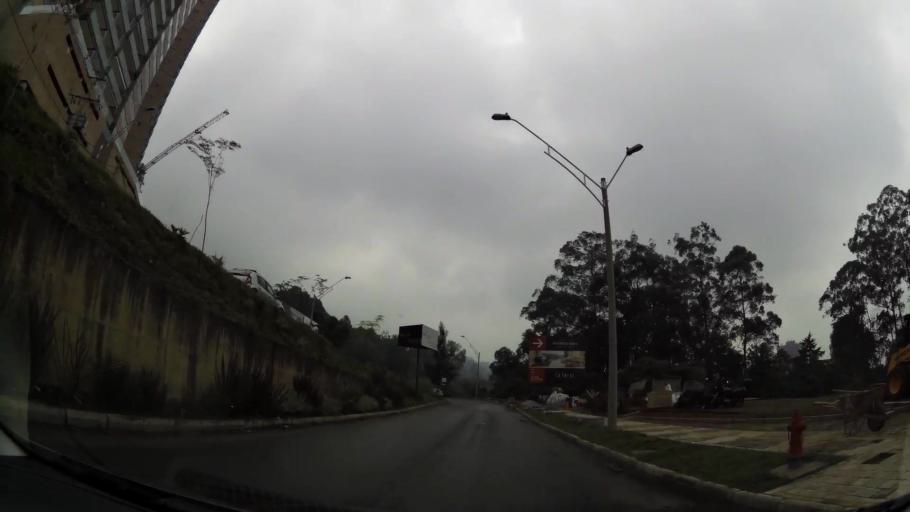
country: CO
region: Antioquia
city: Envigado
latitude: 6.1827
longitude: -75.5587
